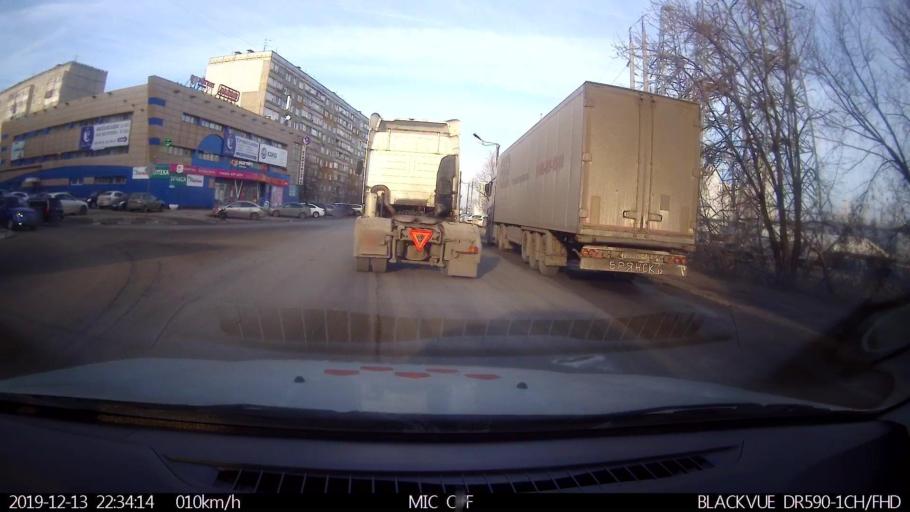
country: RU
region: Nizjnij Novgorod
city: Nizhniy Novgorod
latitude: 56.2903
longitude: 43.9528
